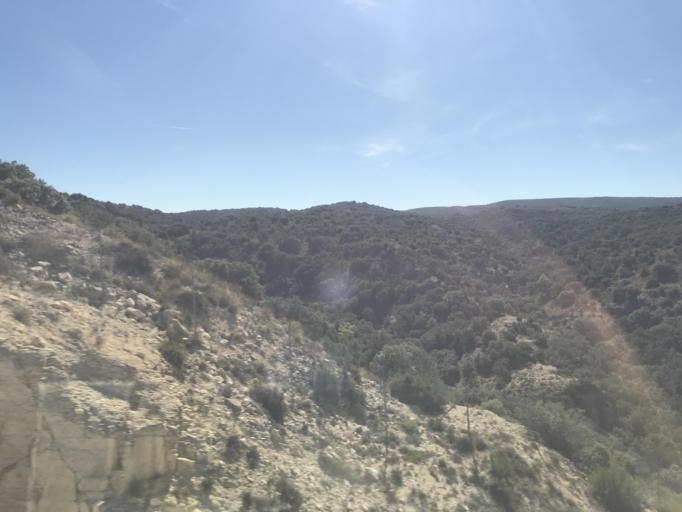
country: ES
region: Castille and Leon
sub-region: Provincia de Soria
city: Arcos de Jalon
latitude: 41.1811
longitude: -2.2077
